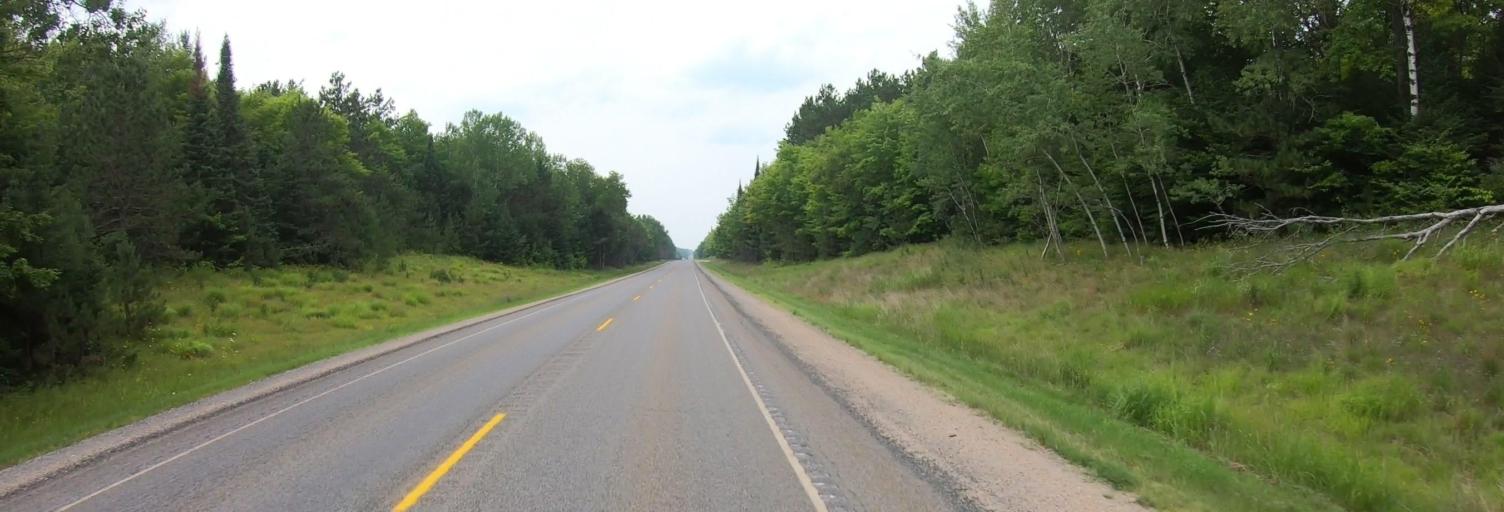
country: US
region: Michigan
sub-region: Alger County
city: Munising
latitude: 46.3331
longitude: -86.7467
